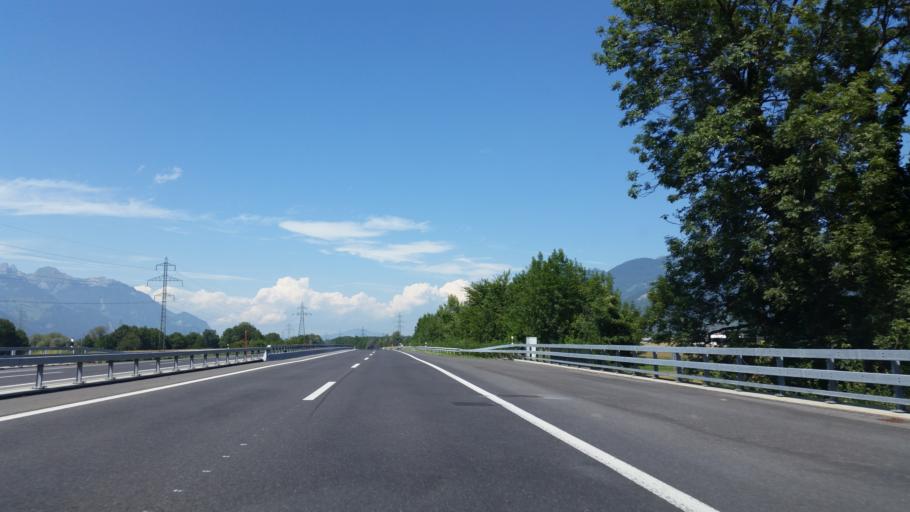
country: CH
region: Vaud
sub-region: Aigle District
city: Bex
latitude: 46.2442
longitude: 6.9949
